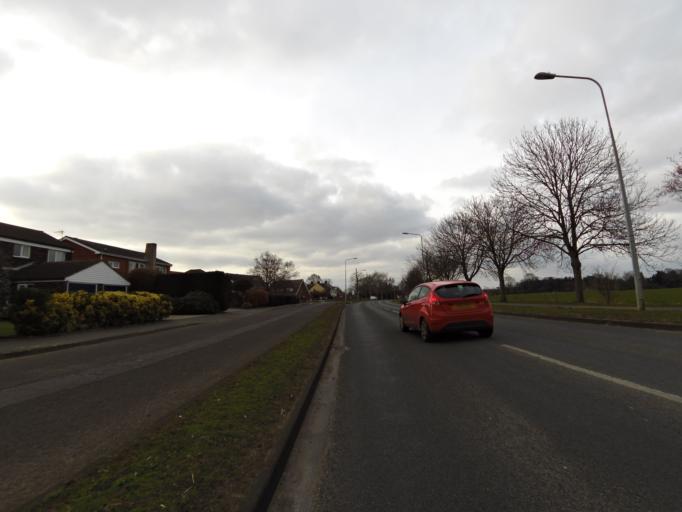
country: GB
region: England
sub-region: Suffolk
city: Ipswich
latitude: 52.0813
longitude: 1.1498
